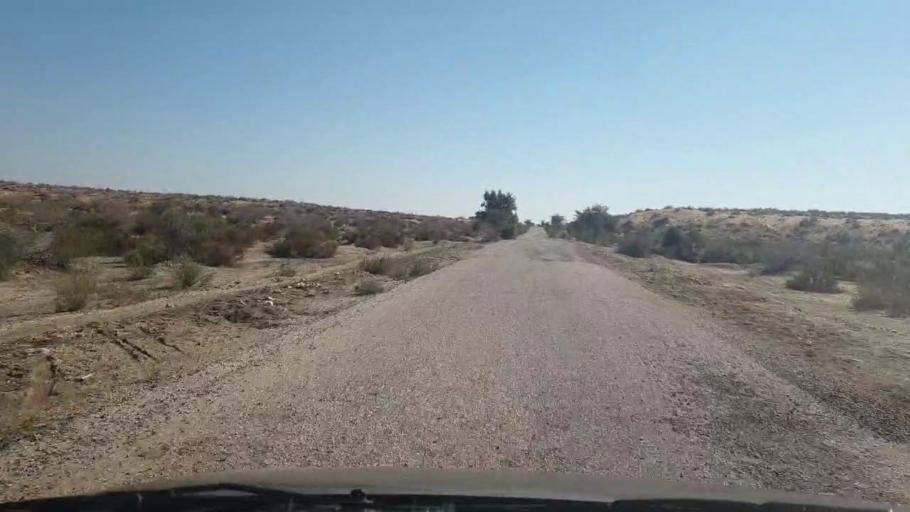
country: PK
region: Sindh
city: Bozdar
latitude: 27.0382
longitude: 68.6931
